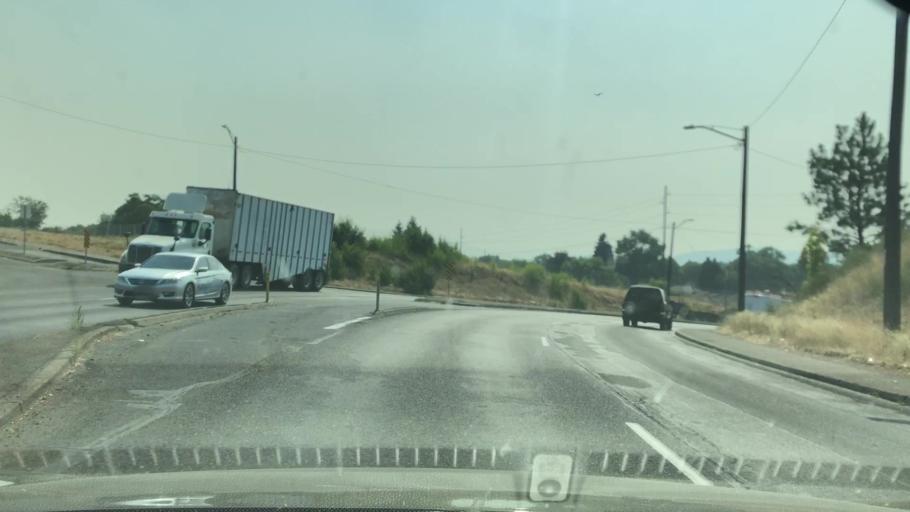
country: US
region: Washington
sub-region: Spokane County
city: Spokane
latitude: 47.6829
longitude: -117.3643
